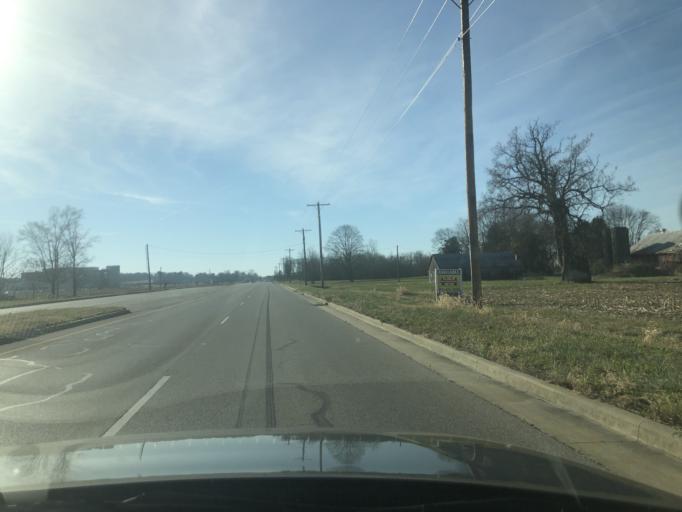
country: US
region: Indiana
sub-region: Warrick County
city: Newburgh
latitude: 37.9882
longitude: -87.4412
